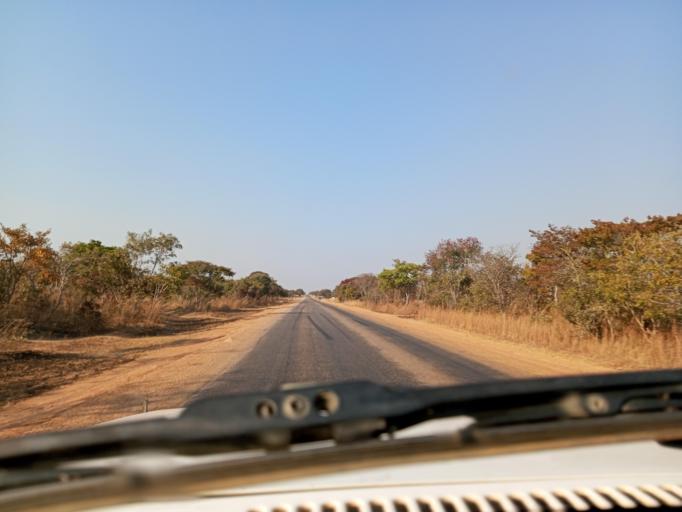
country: ZM
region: Northern
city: Mpika
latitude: -12.3727
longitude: 31.1016
